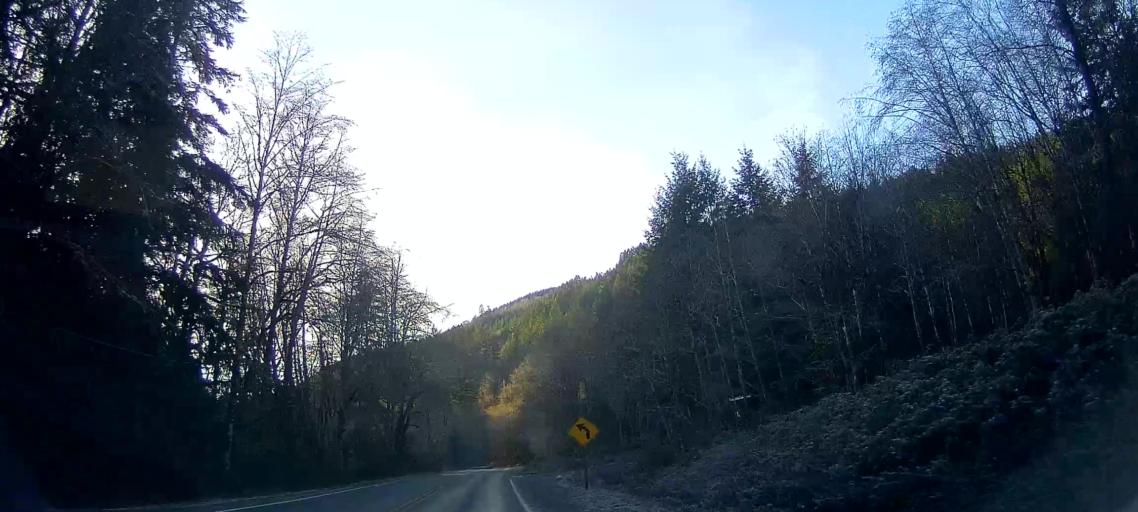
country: US
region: Washington
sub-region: Snohomish County
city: Darrington
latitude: 48.5608
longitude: -121.8333
